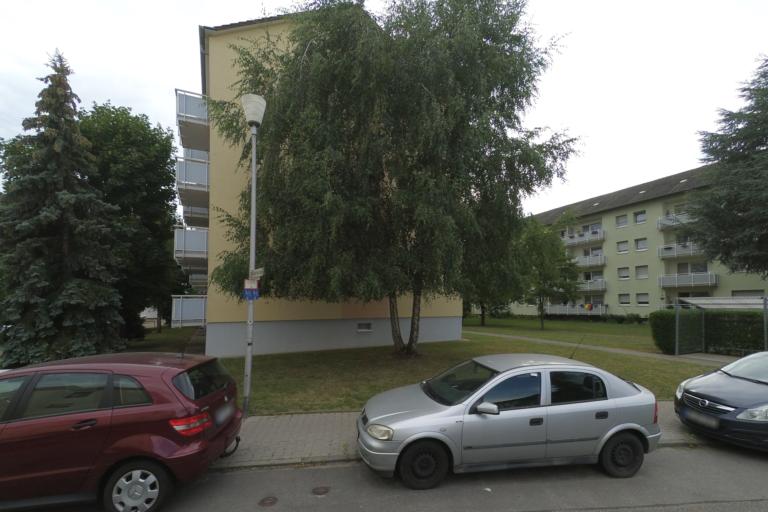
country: DE
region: Hesse
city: Viernheim
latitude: 49.5293
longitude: 8.5630
